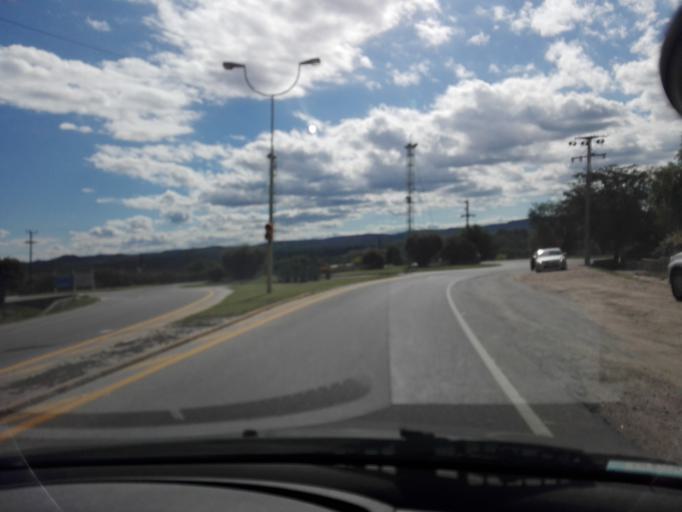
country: AR
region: Cordoba
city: Mina Clavero
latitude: -31.7422
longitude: -65.0046
